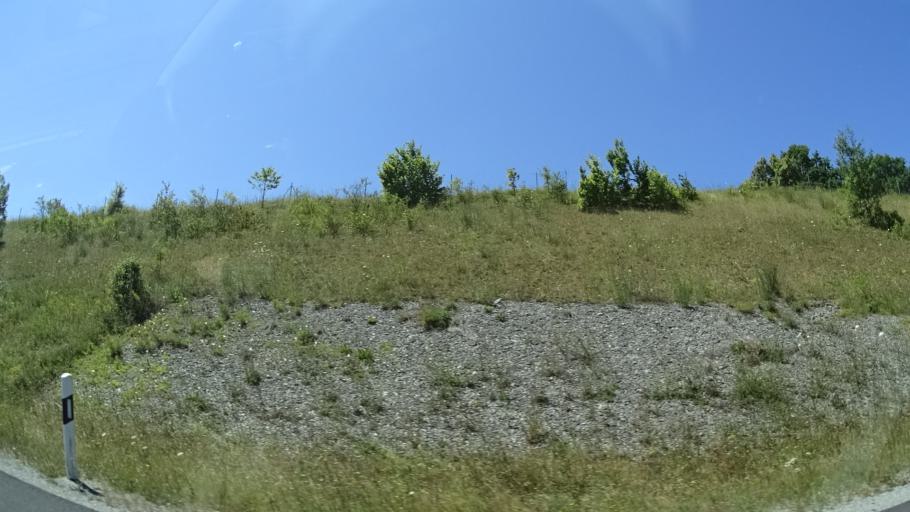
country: DE
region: Bavaria
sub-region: Regierungsbezirk Unterfranken
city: Poppenhausen
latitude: 50.1255
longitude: 10.1508
